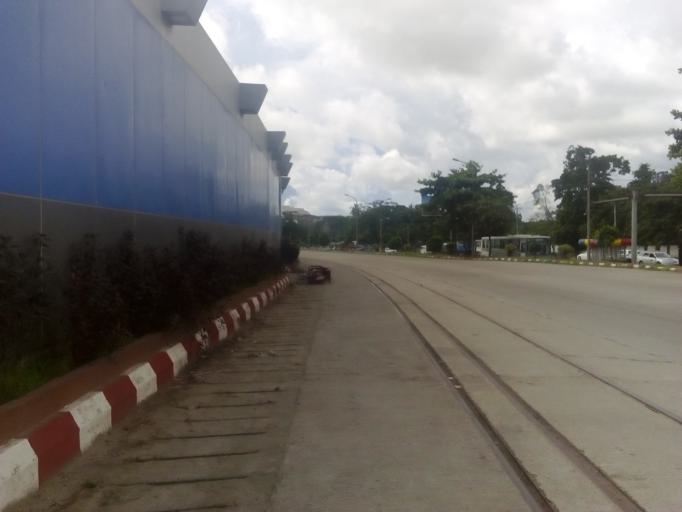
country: MM
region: Yangon
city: Yangon
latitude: 16.7790
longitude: 96.1345
